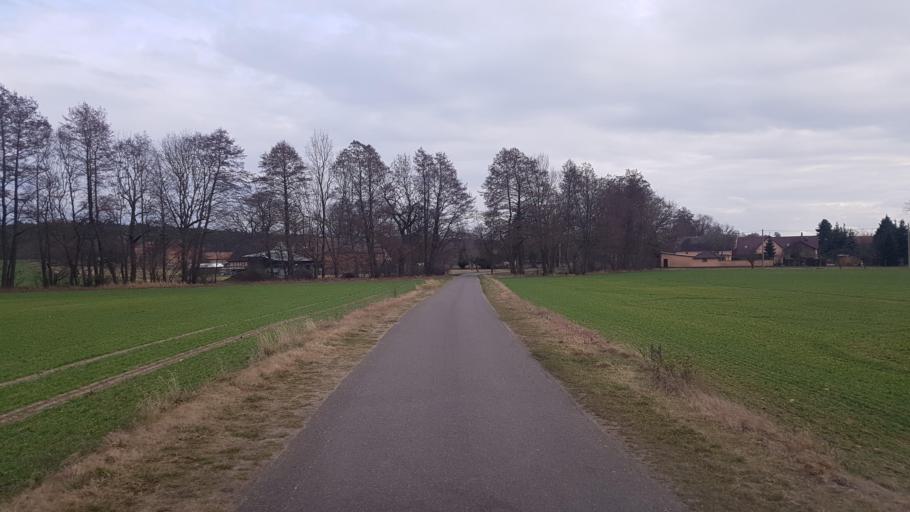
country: DE
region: Brandenburg
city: Golssen
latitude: 51.9441
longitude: 13.6196
